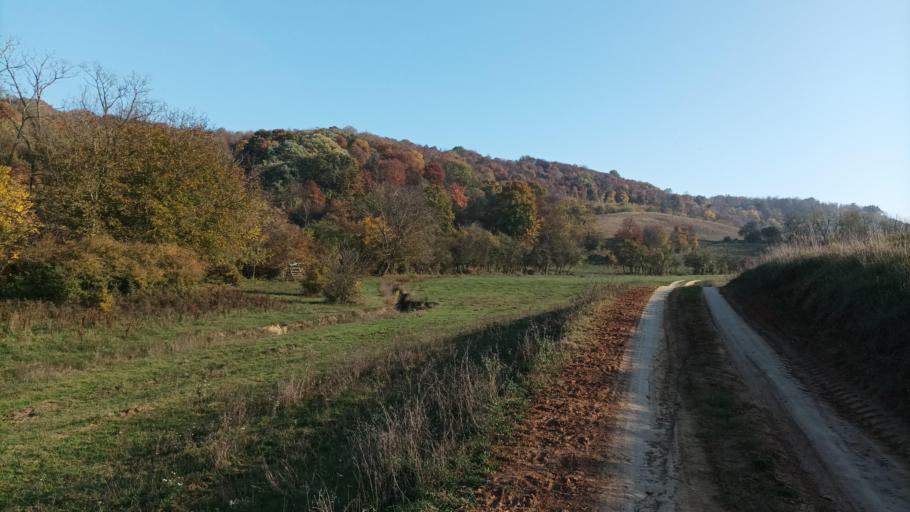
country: HU
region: Tolna
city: Szentgalpuszta
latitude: 46.3356
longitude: 18.6065
